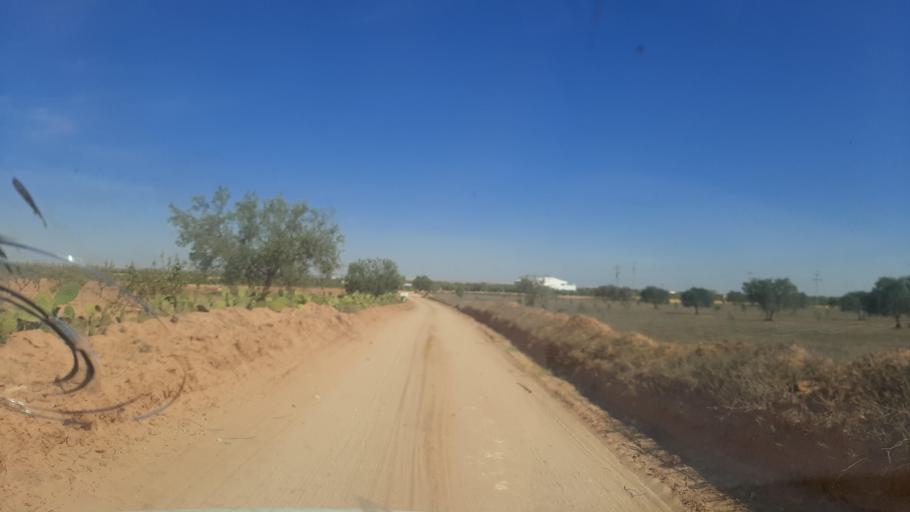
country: TN
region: Safaqis
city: Sfax
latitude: 34.8820
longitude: 10.5775
